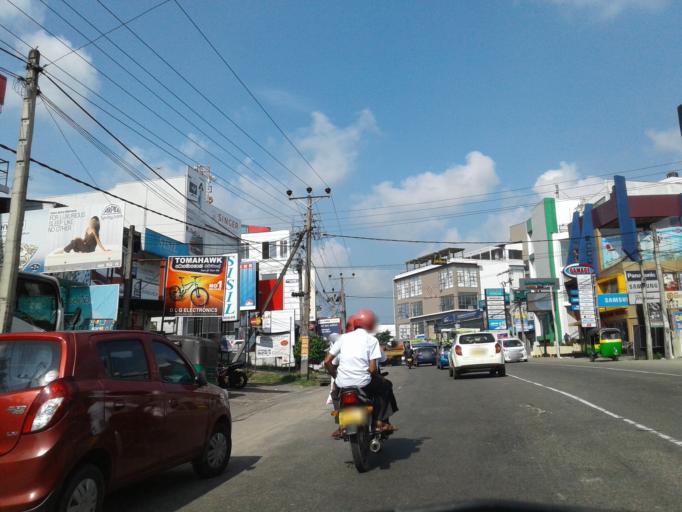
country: LK
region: Western
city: Battaramulla South
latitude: 6.9046
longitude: 79.9531
